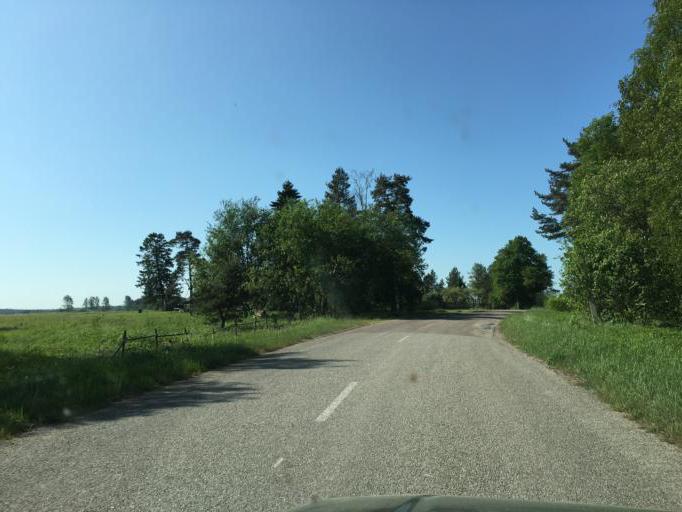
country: LV
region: Ventspils
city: Ventspils
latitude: 57.5045
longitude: 21.8475
